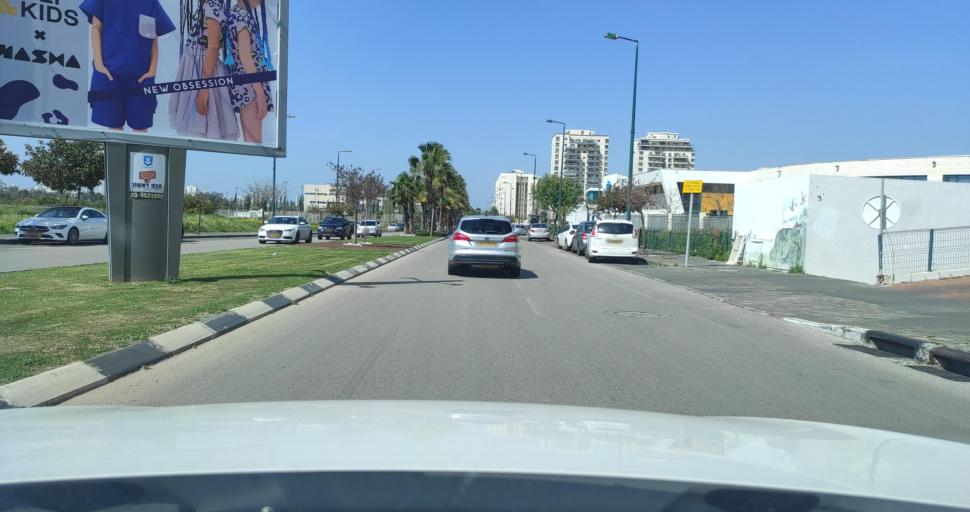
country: IL
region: Central District
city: Nordiyya
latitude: 32.3029
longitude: 34.8696
